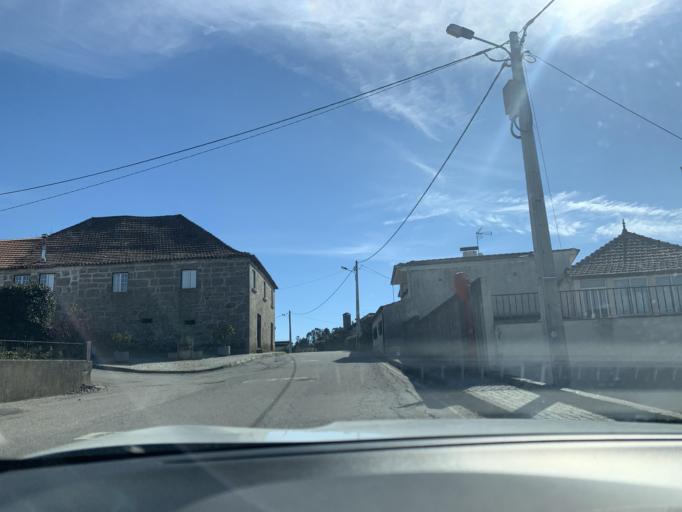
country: PT
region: Viseu
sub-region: Concelho de Tondela
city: Tondela
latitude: 40.5877
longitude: -8.0256
